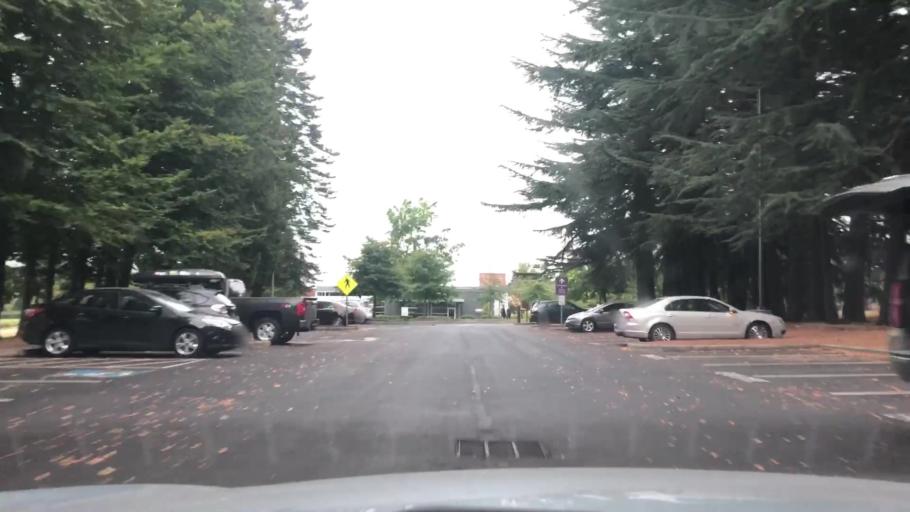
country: US
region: Oregon
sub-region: Multnomah County
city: Lents
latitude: 45.5429
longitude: -122.5258
